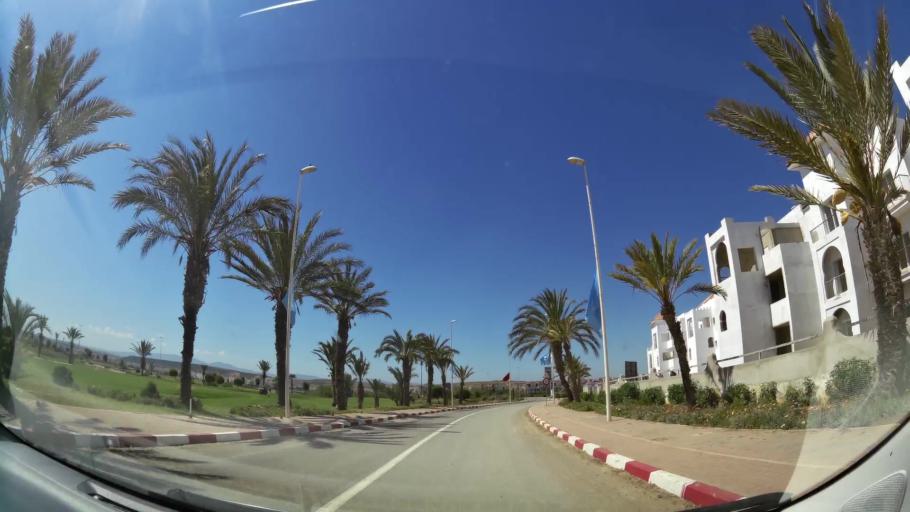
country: MA
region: Oriental
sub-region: Berkane-Taourirt
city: Madagh
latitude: 35.1092
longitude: -2.3107
